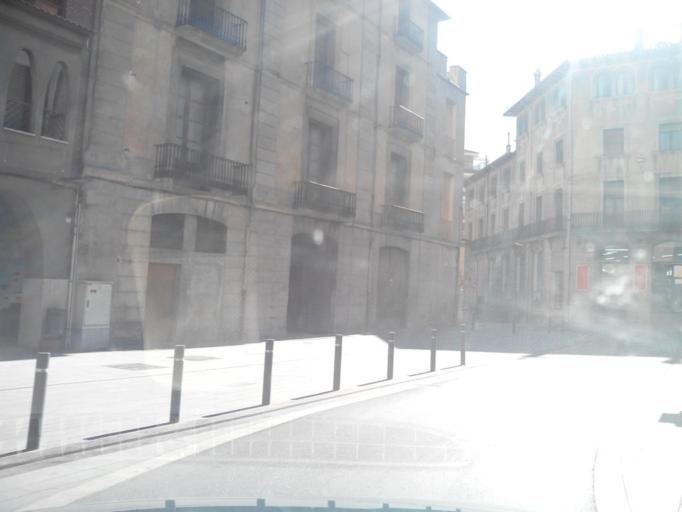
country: ES
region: Catalonia
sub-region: Provincia de Girona
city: Ripoll
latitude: 42.1987
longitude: 2.1912
